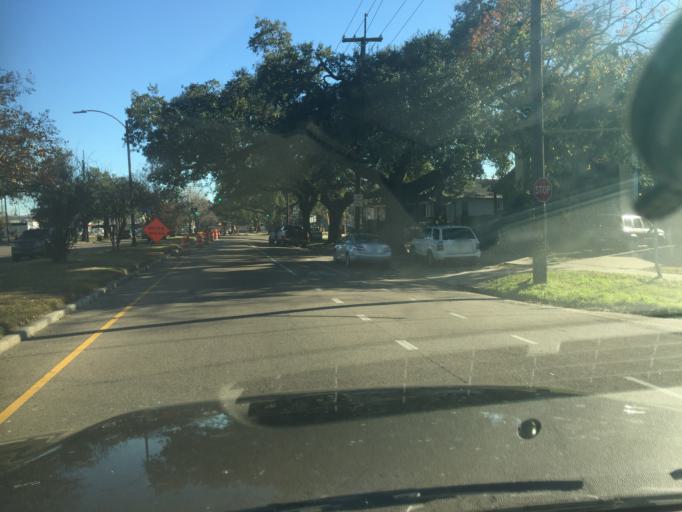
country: US
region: Louisiana
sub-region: Orleans Parish
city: New Orleans
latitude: 29.9792
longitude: -90.0695
